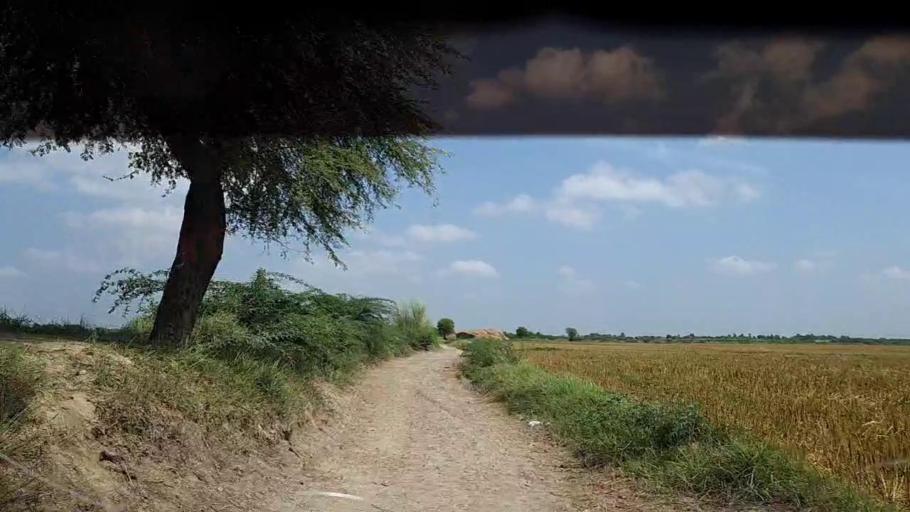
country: PK
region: Sindh
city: Kadhan
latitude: 24.5830
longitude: 68.9676
